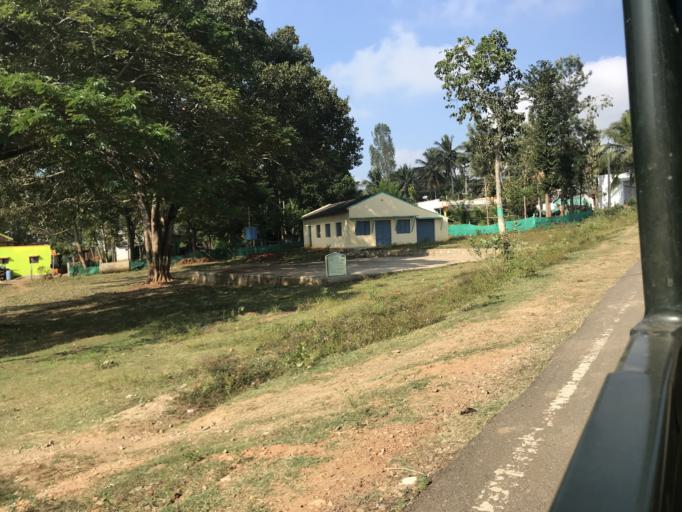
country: IN
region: Karnataka
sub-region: Mysore
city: Heggadadevankote
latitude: 11.9472
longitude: 76.2580
